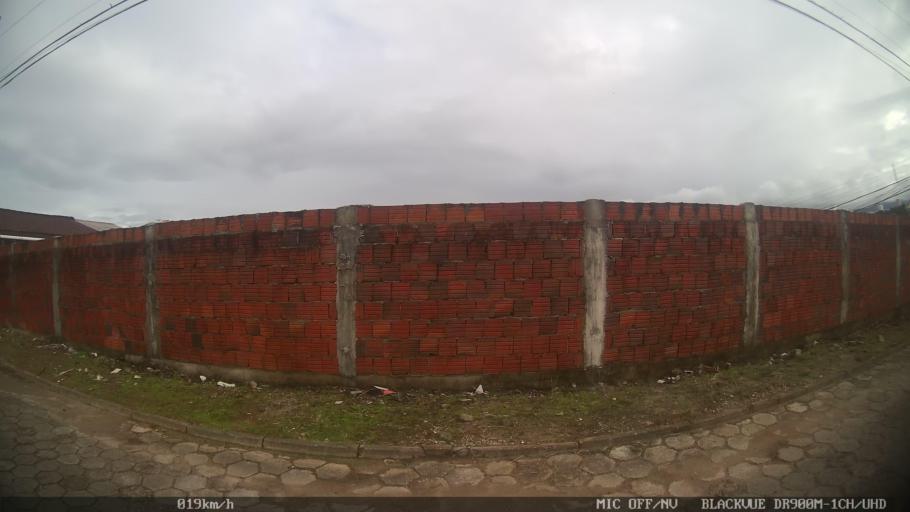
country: BR
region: Santa Catarina
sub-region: Sao Jose
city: Campinas
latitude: -27.5481
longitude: -48.6307
